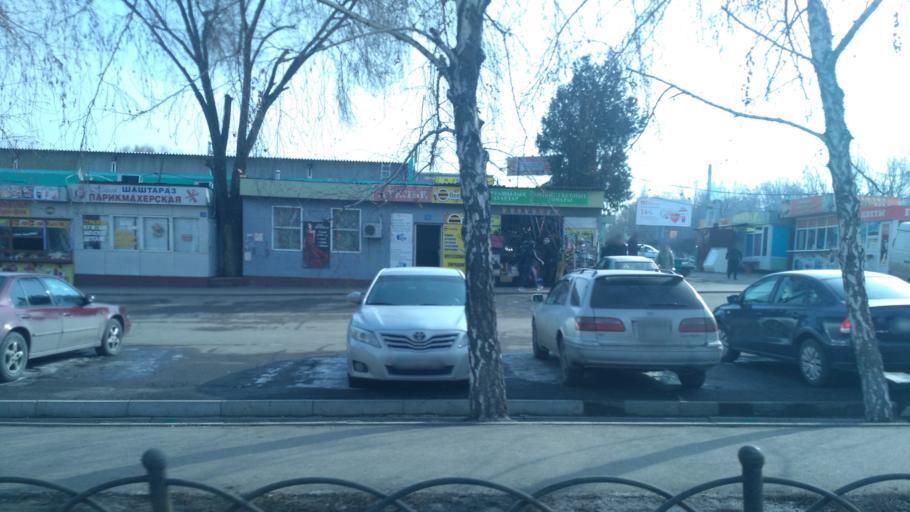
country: KZ
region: Almaty Qalasy
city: Almaty
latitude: 43.2304
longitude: 76.8334
